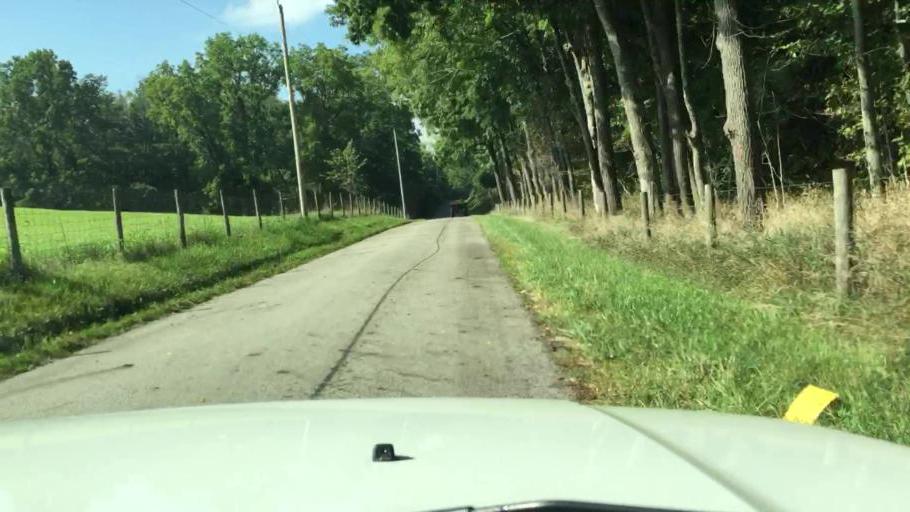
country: US
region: Ohio
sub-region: Champaign County
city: Mechanicsburg
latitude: 40.0058
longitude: -83.6534
